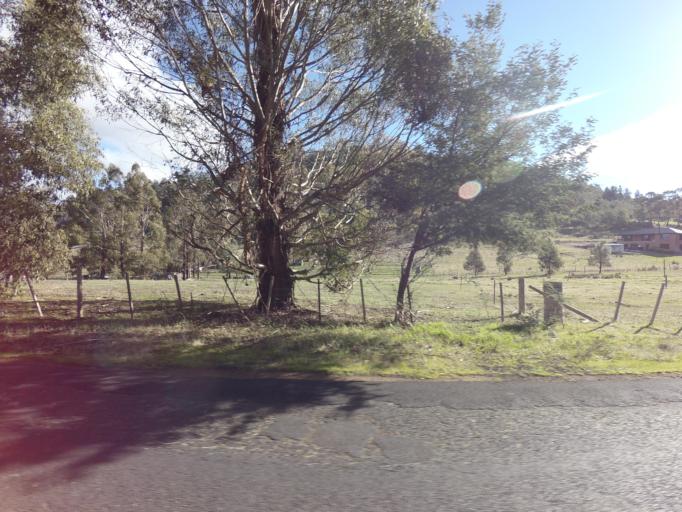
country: AU
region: Tasmania
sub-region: Derwent Valley
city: New Norfolk
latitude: -42.7507
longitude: 147.0460
